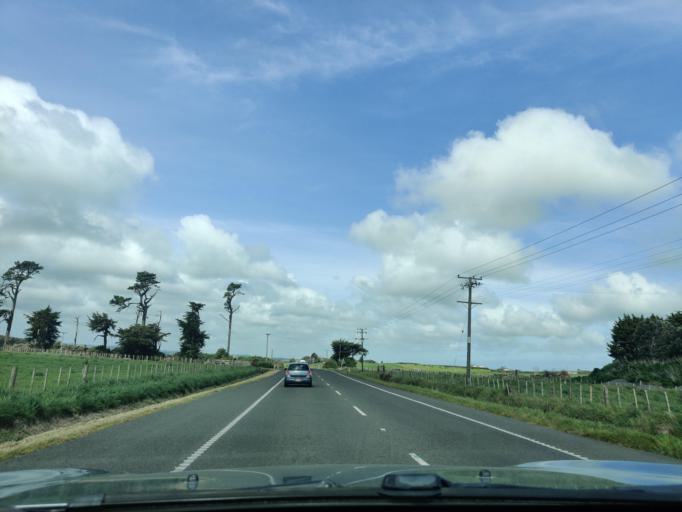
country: NZ
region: Taranaki
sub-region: South Taranaki District
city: Patea
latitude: -39.7738
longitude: 174.6763
